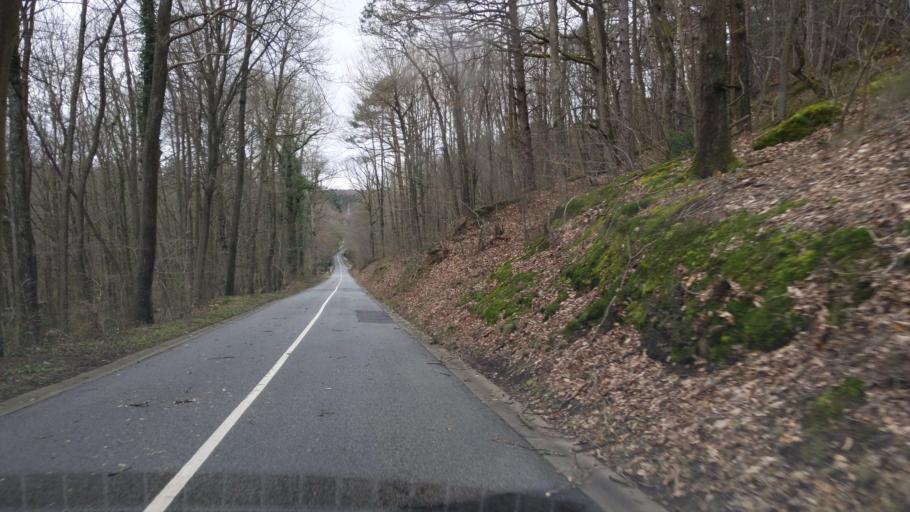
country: FR
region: Ile-de-France
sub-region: Departement des Yvelines
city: Chevreuse
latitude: 48.6848
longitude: 2.0254
